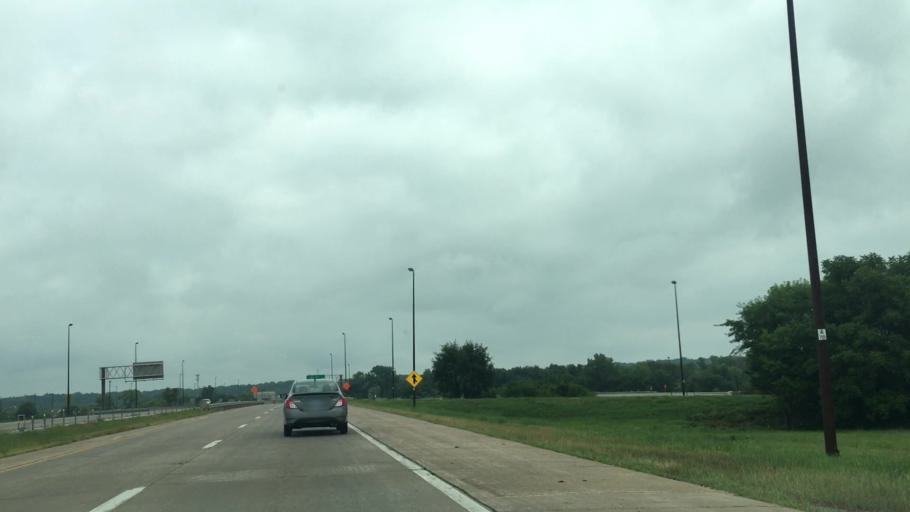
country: US
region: Illinois
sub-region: Rock Island County
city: Coal Valley
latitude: 41.4559
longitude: -90.4951
